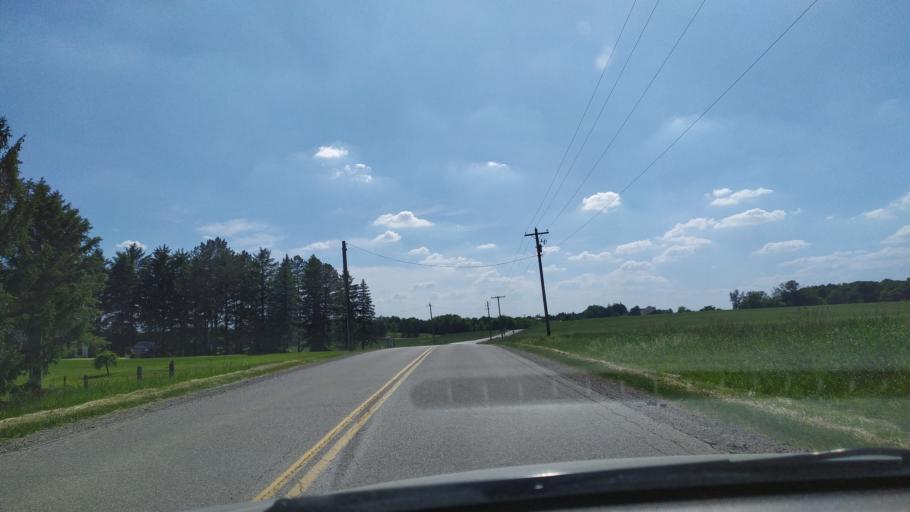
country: CA
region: Ontario
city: Kitchener
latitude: 43.3589
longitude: -80.6445
